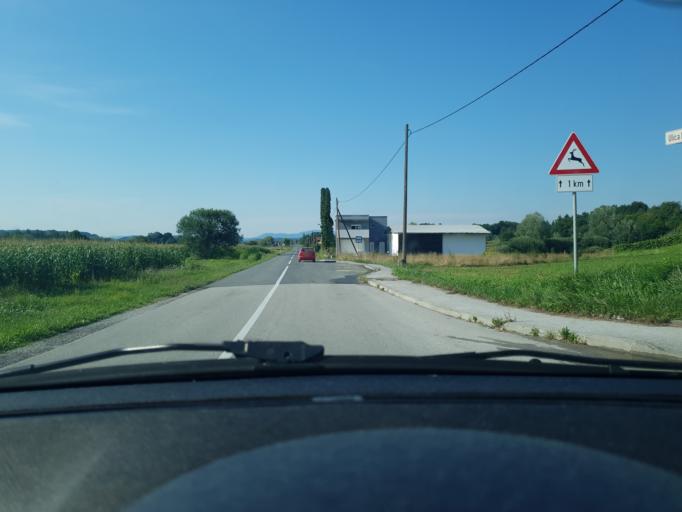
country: HR
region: Zagrebacka
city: Jakovlje
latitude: 45.9598
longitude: 15.8550
